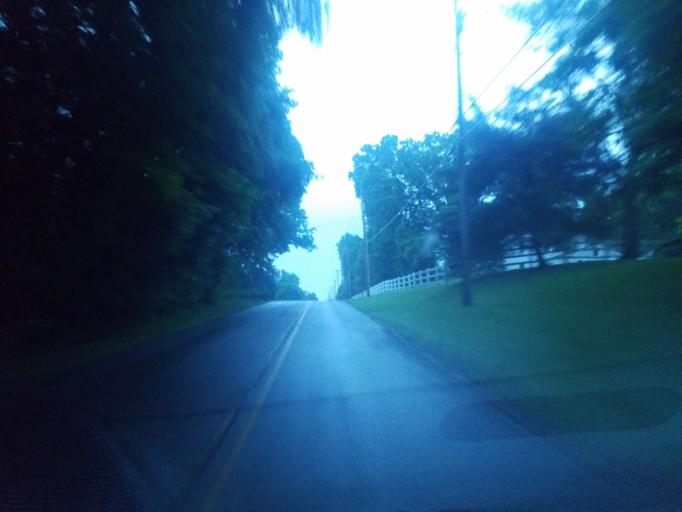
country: US
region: Ohio
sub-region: Mahoning County
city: Boardman
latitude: 41.0030
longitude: -80.7114
